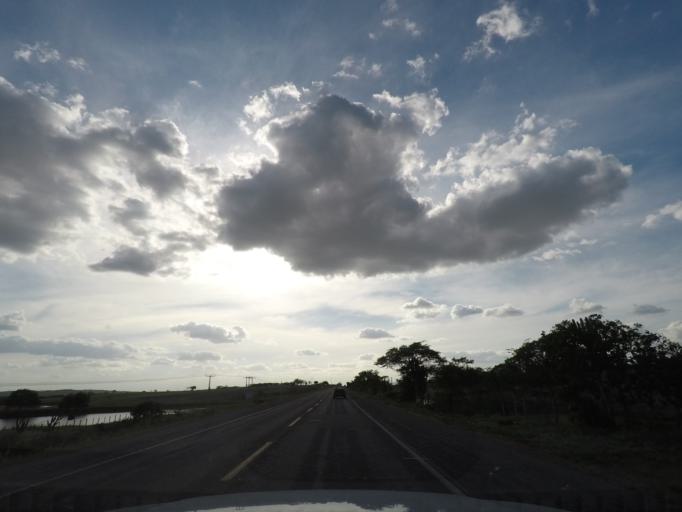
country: BR
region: Bahia
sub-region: Anguera
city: Anguera
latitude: -12.1864
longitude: -39.4844
